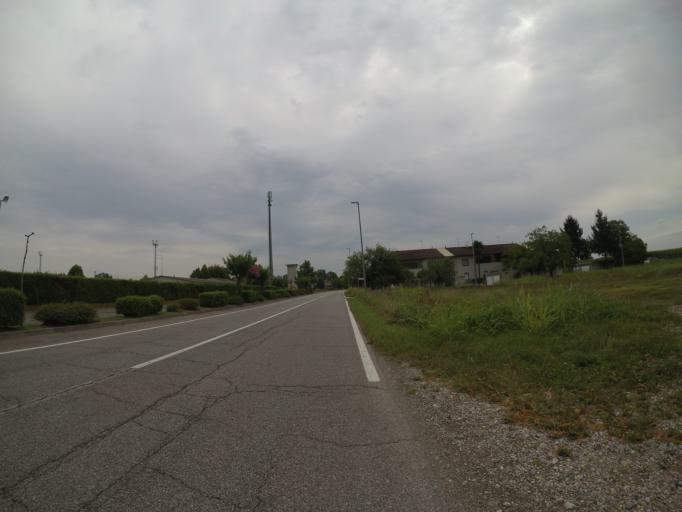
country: IT
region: Friuli Venezia Giulia
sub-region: Provincia di Udine
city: Varmo
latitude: 45.8852
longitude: 12.9943
